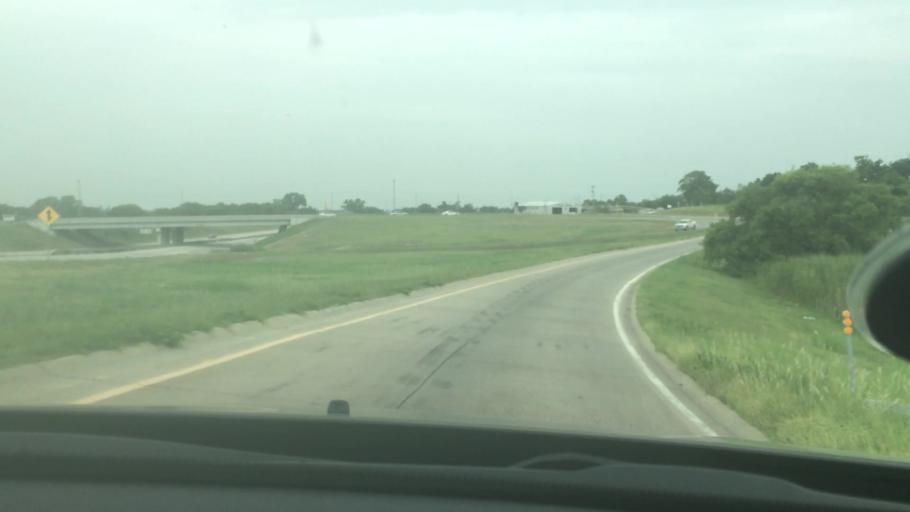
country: US
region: Oklahoma
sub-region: Pontotoc County
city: Ada
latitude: 34.7625
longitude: -96.6994
